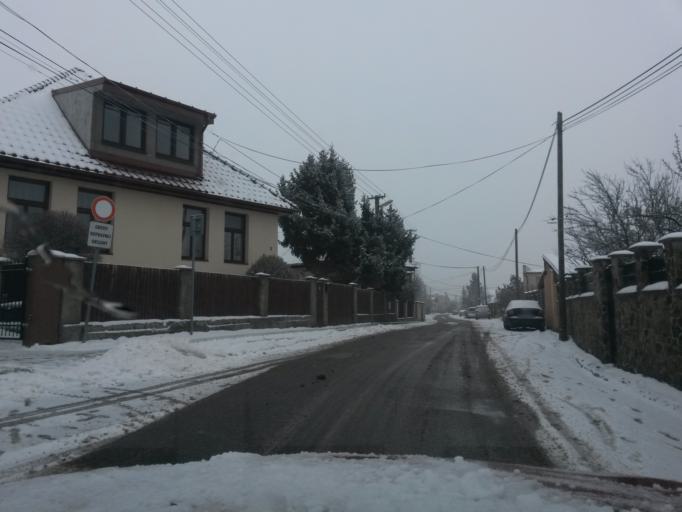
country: SK
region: Kosicky
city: Kosice
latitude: 48.7334
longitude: 21.2980
